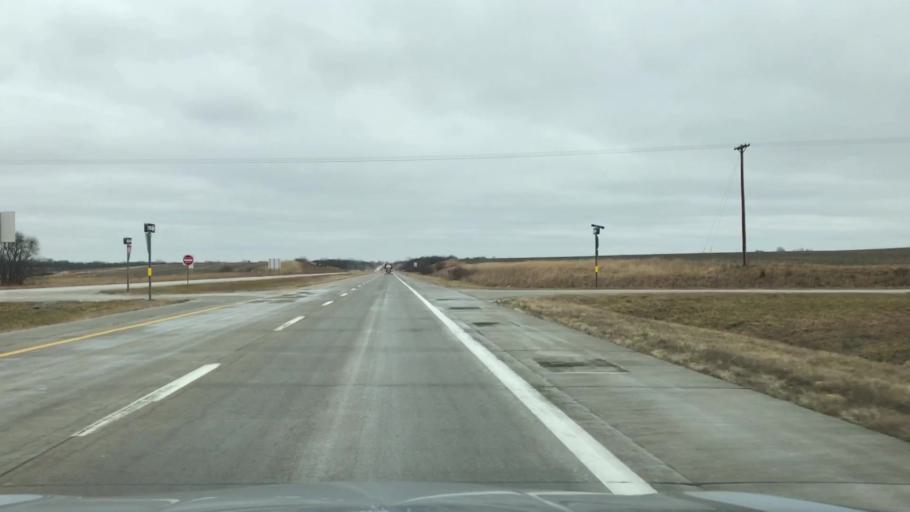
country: US
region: Missouri
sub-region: Caldwell County
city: Hamilton
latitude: 39.7338
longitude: -93.9843
